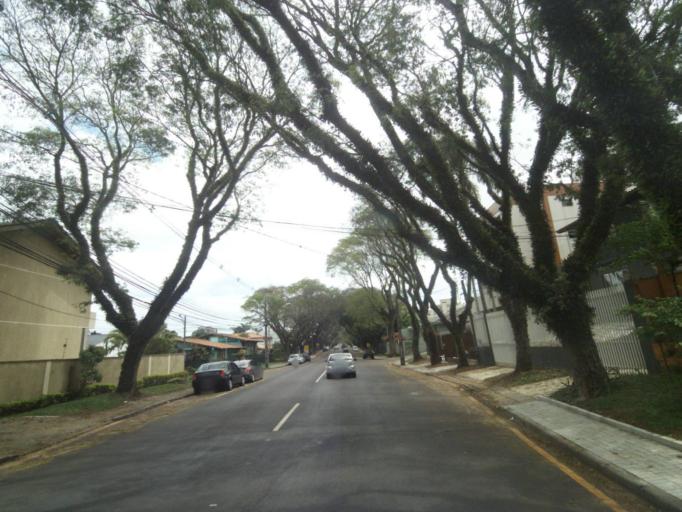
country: BR
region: Parana
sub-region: Curitiba
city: Curitiba
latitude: -25.4128
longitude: -49.2342
